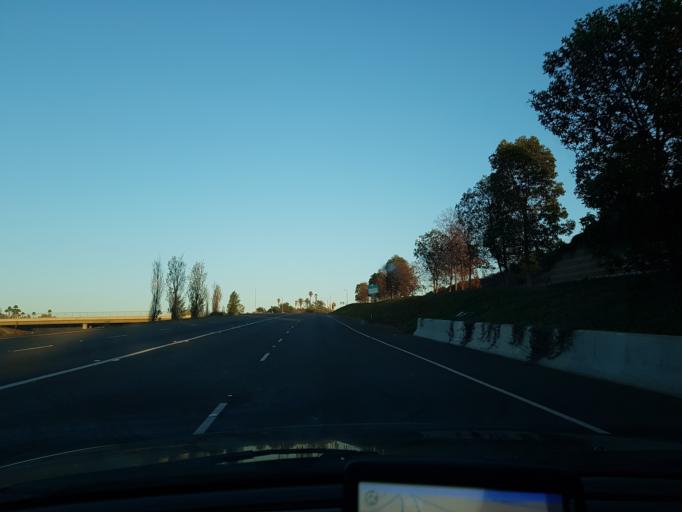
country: US
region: California
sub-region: San Diego County
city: Fairbanks Ranch
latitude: 32.9532
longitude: -117.1330
